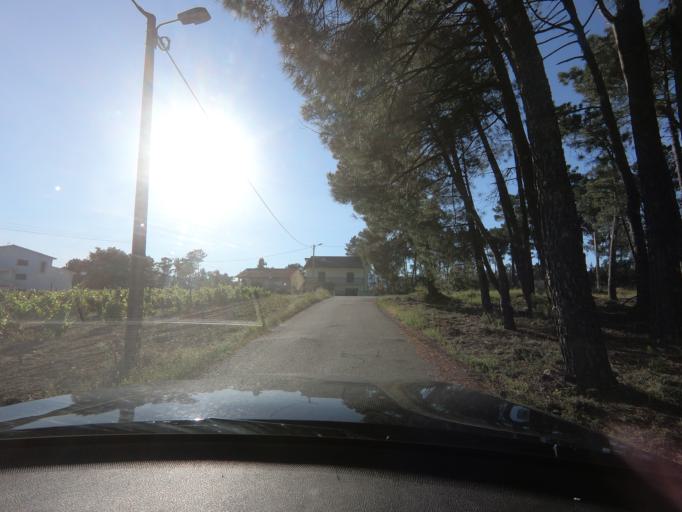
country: PT
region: Vila Real
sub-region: Vila Real
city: Vila Real
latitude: 41.3162
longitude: -7.6875
